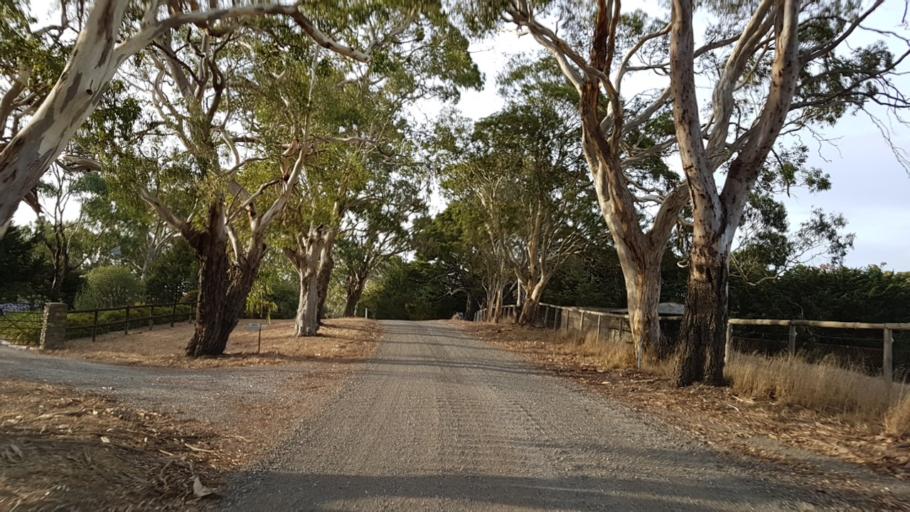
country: AU
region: South Australia
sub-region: Mount Barker
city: Nairne
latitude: -35.0042
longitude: 138.9111
